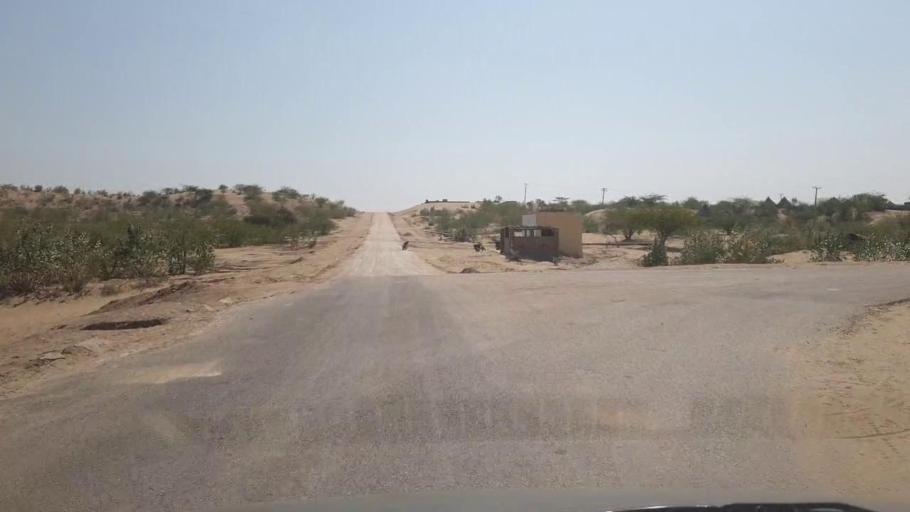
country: PK
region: Sindh
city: Chor
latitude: 25.5771
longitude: 70.1911
